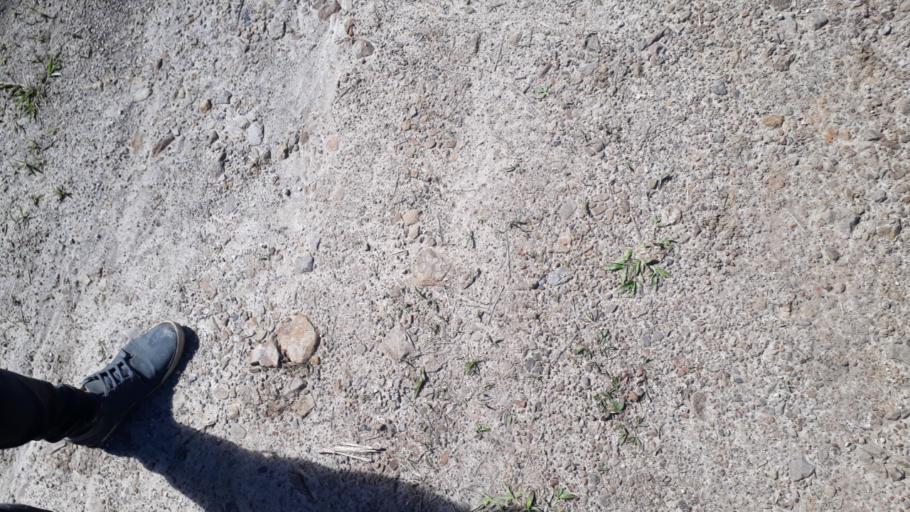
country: CO
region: Casanare
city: Nunchia
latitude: 5.6702
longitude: -72.4307
